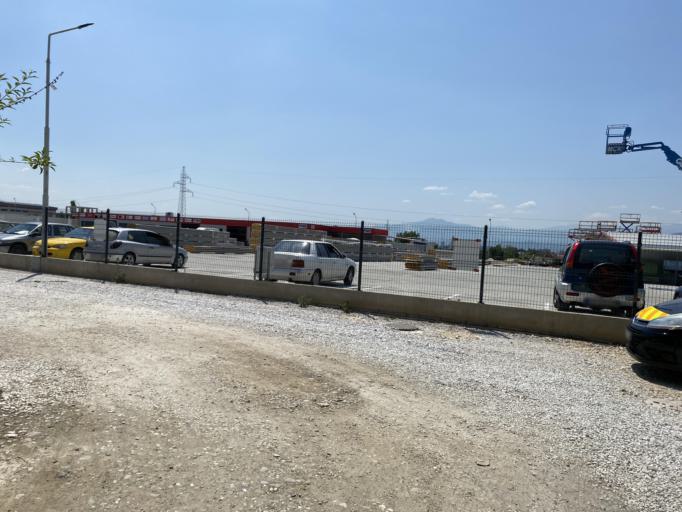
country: MK
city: Radishani
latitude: 42.0467
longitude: 21.4454
